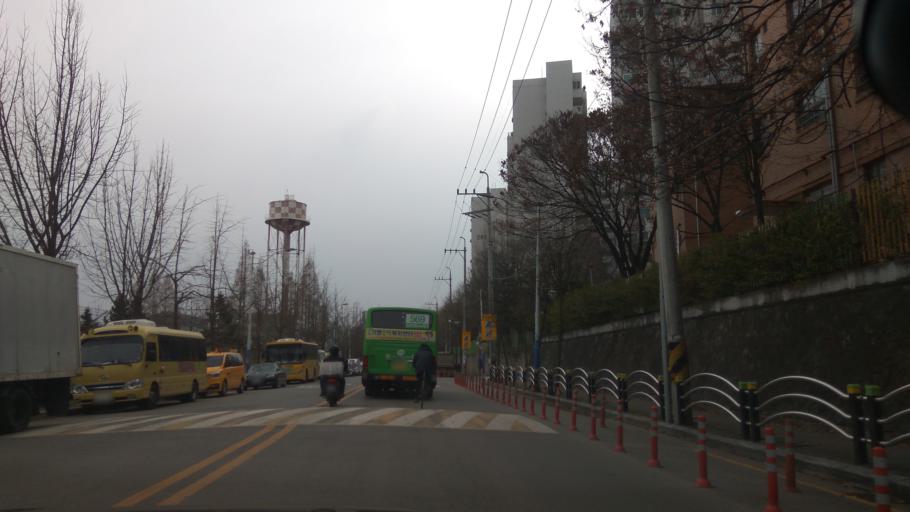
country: KR
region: Incheon
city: Incheon
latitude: 37.4936
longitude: 126.7099
